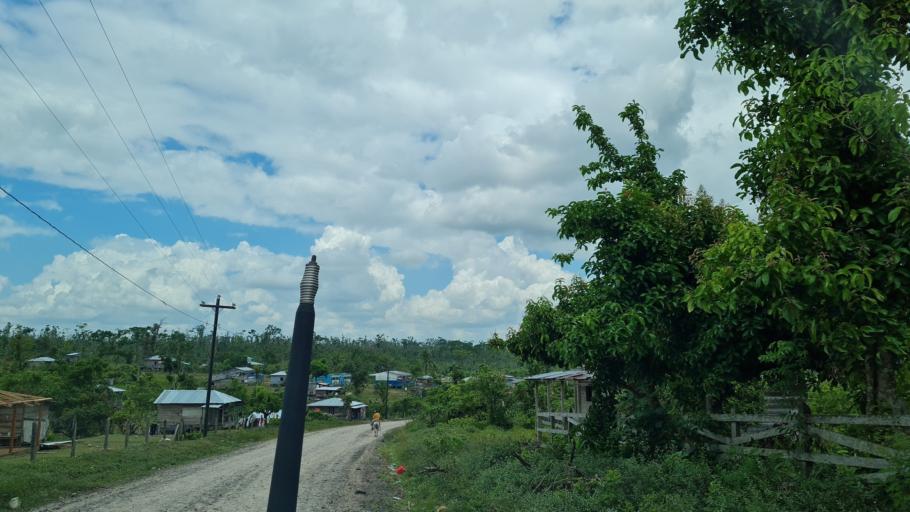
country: NI
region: Atlantico Norte (RAAN)
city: Siuna
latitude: 13.5900
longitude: -84.3397
